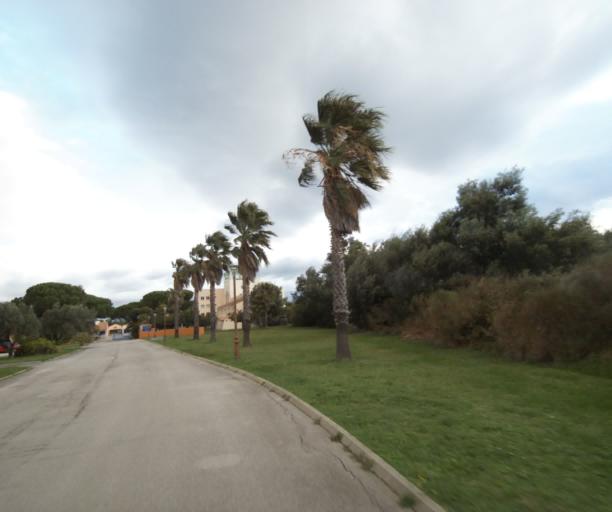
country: FR
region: Languedoc-Roussillon
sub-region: Departement des Pyrenees-Orientales
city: Argelers
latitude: 42.5635
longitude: 3.0113
